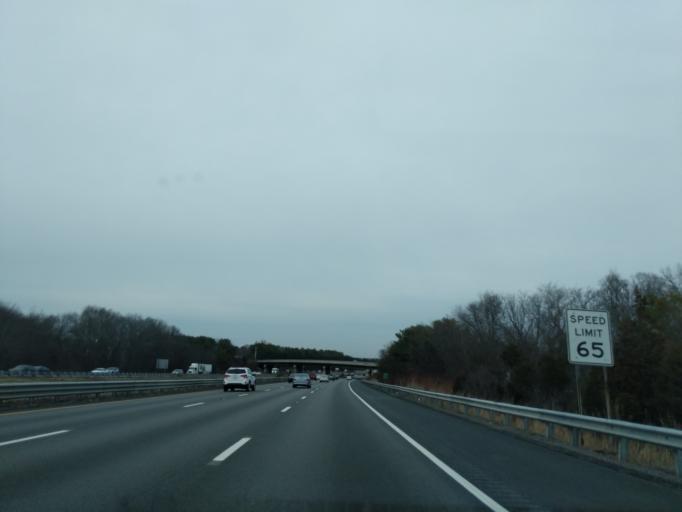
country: US
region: Massachusetts
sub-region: Norfolk County
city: Plainville
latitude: 41.9932
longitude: -71.2924
